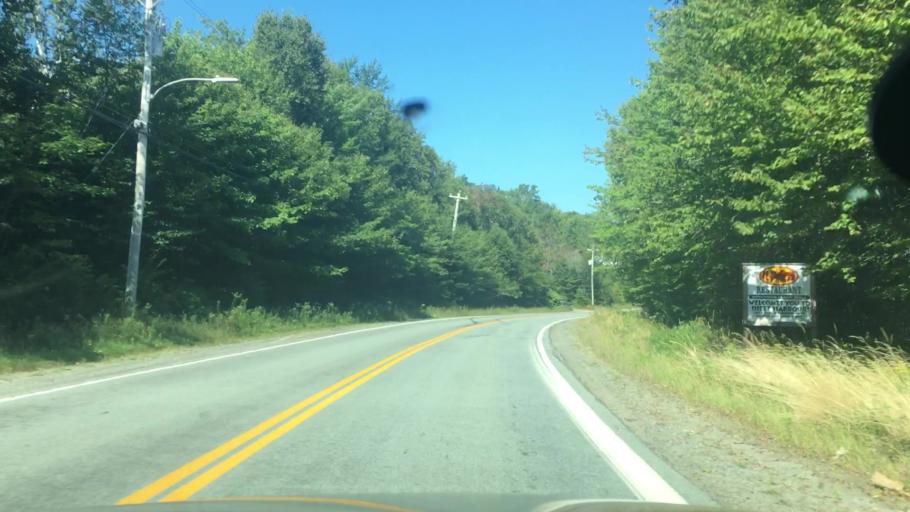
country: CA
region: Nova Scotia
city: New Glasgow
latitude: 44.9183
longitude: -62.5418
